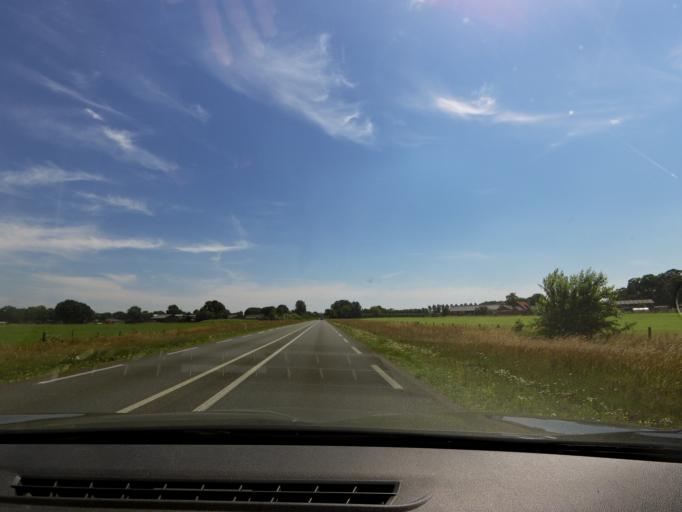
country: NL
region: Overijssel
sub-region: Gemeente Wierden
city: Wierden
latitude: 52.3169
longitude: 6.5463
